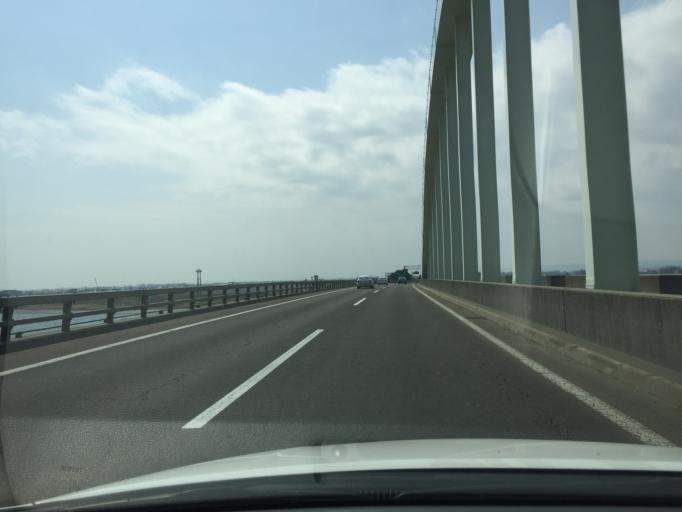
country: JP
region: Miyagi
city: Sendai
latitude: 38.1901
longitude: 140.9384
